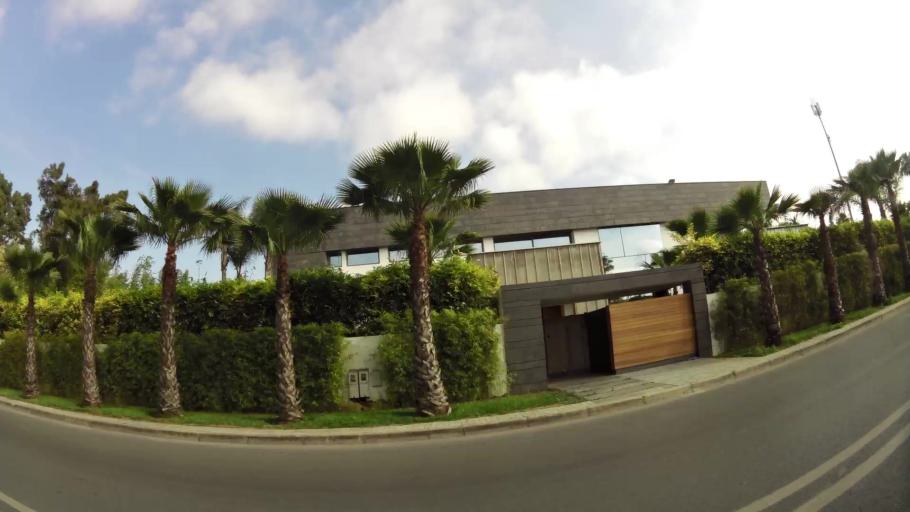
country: MA
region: Rabat-Sale-Zemmour-Zaer
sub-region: Rabat
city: Rabat
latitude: 33.9596
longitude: -6.8418
